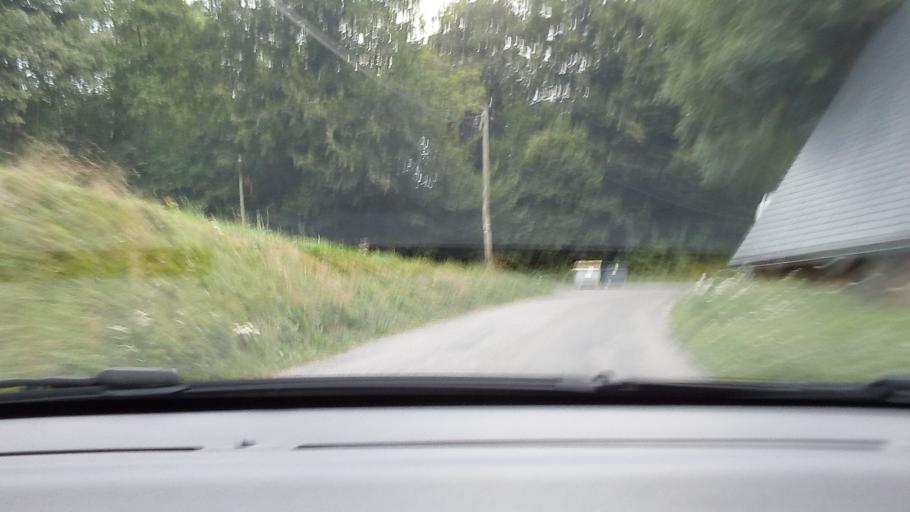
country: FR
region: Midi-Pyrenees
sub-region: Departement des Hautes-Pyrenees
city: Cauterets
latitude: 42.9439
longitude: -0.1833
